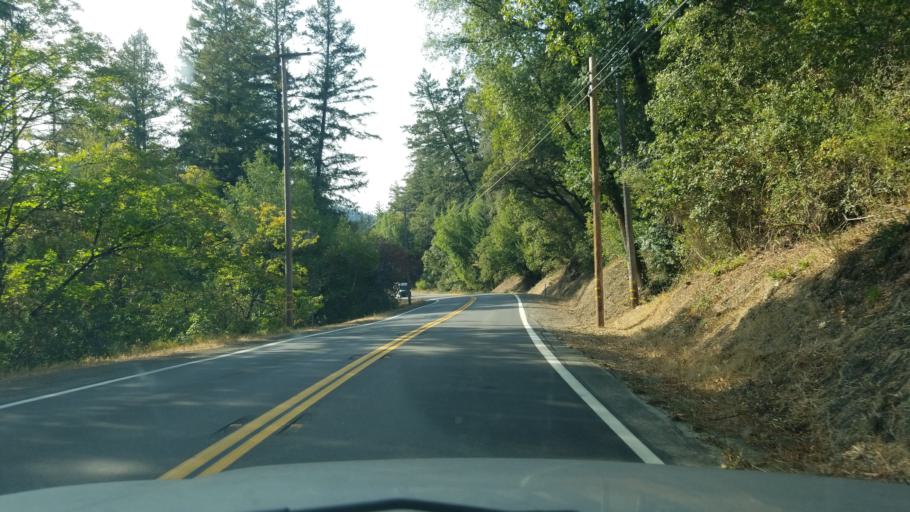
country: US
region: California
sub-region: Humboldt County
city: Redway
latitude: 40.2201
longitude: -123.8169
